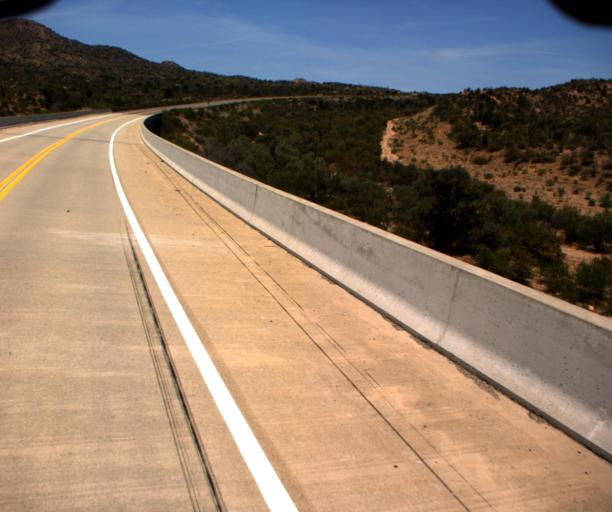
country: US
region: Arizona
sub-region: Gila County
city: Claypool
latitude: 33.5245
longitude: -110.9092
